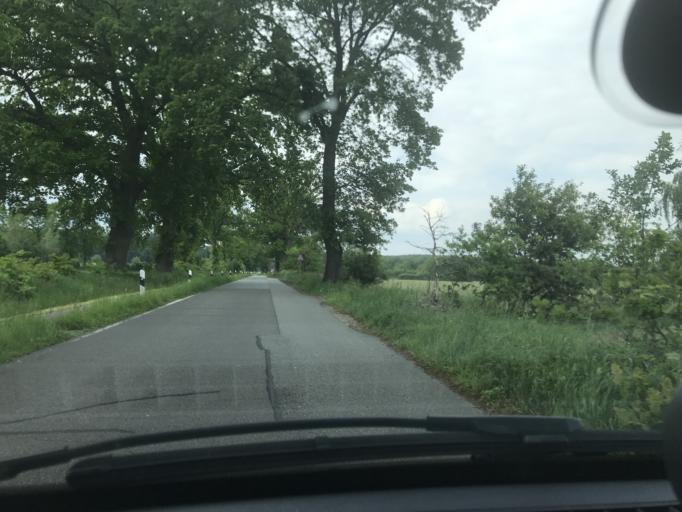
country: DE
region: Schleswig-Holstein
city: Witzhave
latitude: 53.5812
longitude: 10.3404
